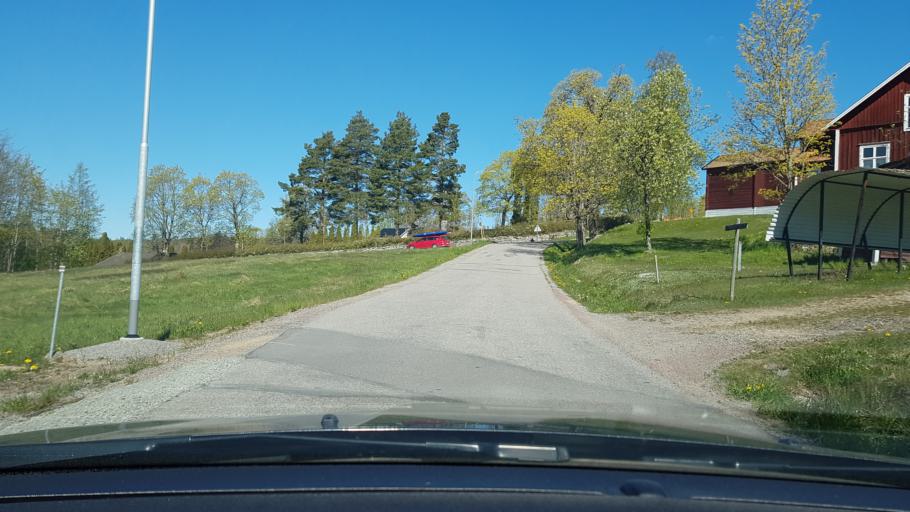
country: SE
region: Dalarna
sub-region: Faluns Kommun
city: Bjursas
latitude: 60.7364
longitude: 15.4503
